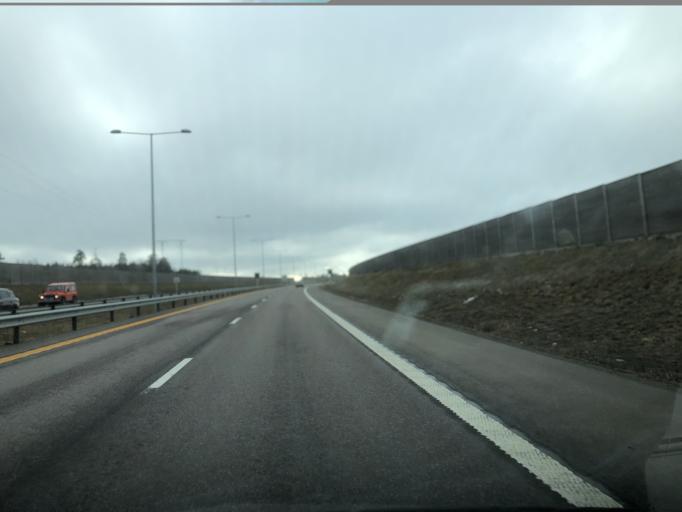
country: NO
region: Vestfold
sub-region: Sandefjord
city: Sandefjord
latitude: 59.1460
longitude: 10.1741
